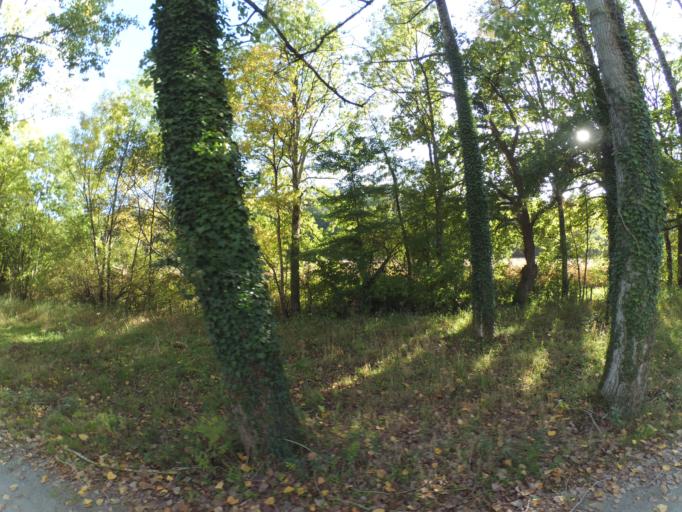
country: FR
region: Brittany
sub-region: Departement du Morbihan
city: Saint-Vincent-sur-Oust
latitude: 47.7221
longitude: -2.1802
